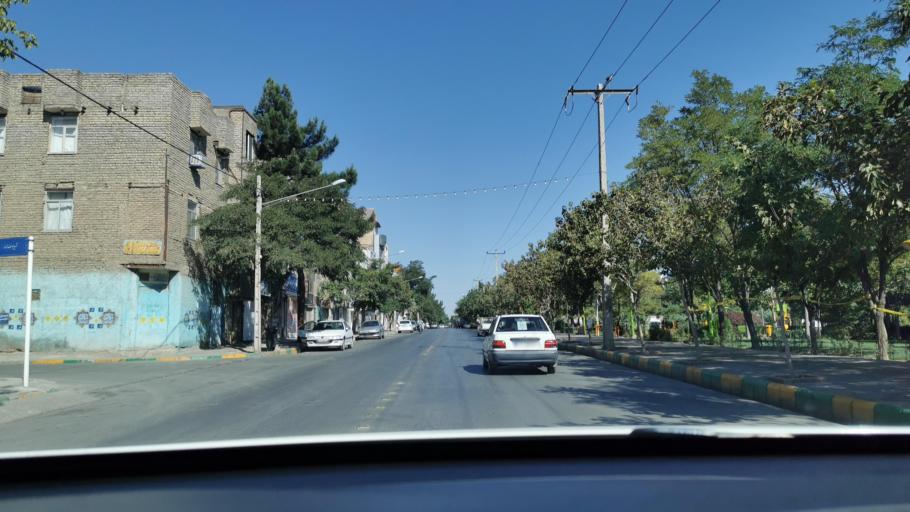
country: IR
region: Razavi Khorasan
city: Mashhad
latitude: 36.3330
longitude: 59.6413
